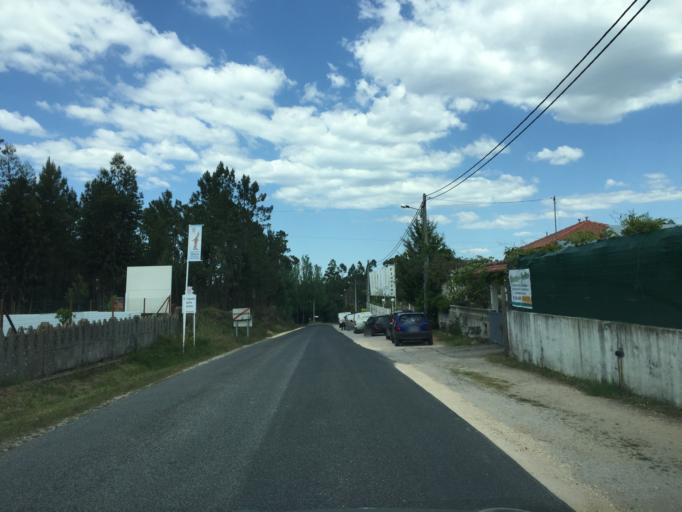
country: PT
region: Santarem
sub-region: Ourem
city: Ourem
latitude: 39.6913
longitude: -8.5432
